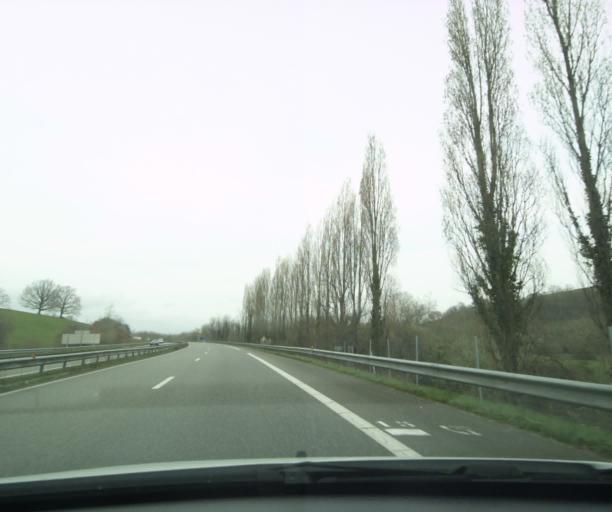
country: FR
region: Aquitaine
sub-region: Departement des Pyrenees-Atlantiques
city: Urt
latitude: 43.4582
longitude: -1.2925
